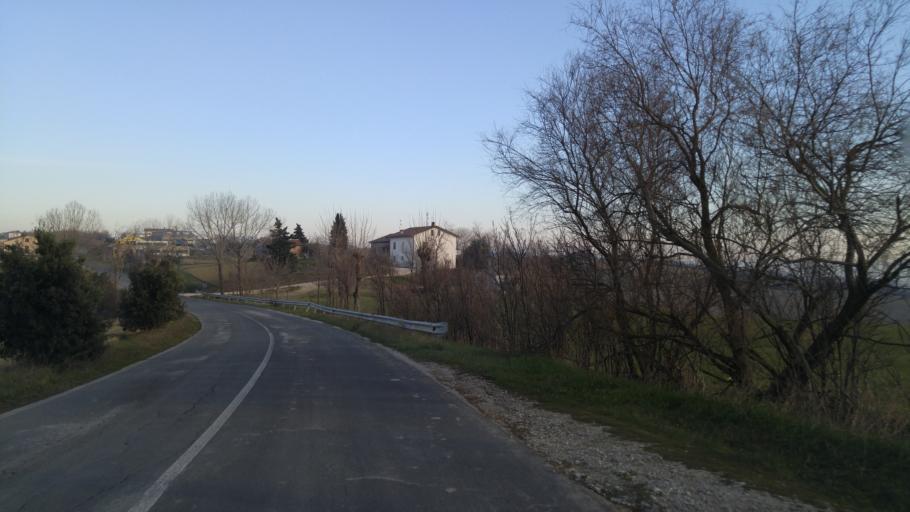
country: IT
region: The Marches
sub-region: Provincia di Pesaro e Urbino
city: San Giorgio di Pesaro
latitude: 43.7099
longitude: 12.9904
